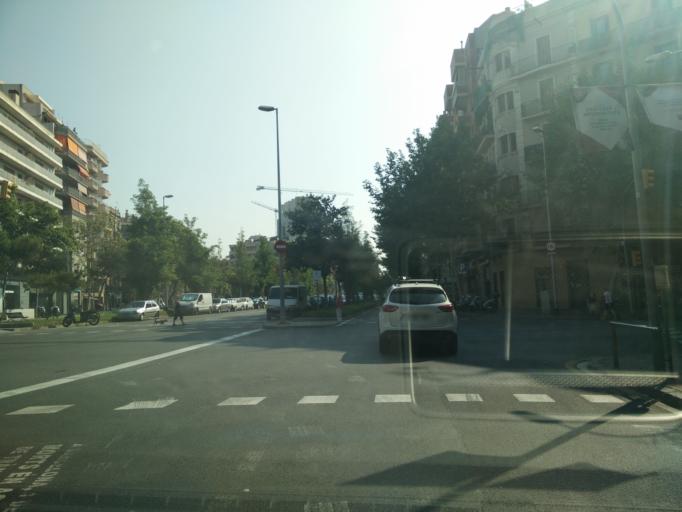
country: ES
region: Catalonia
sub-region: Provincia de Barcelona
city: Sants-Montjuic
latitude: 41.3820
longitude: 2.1471
